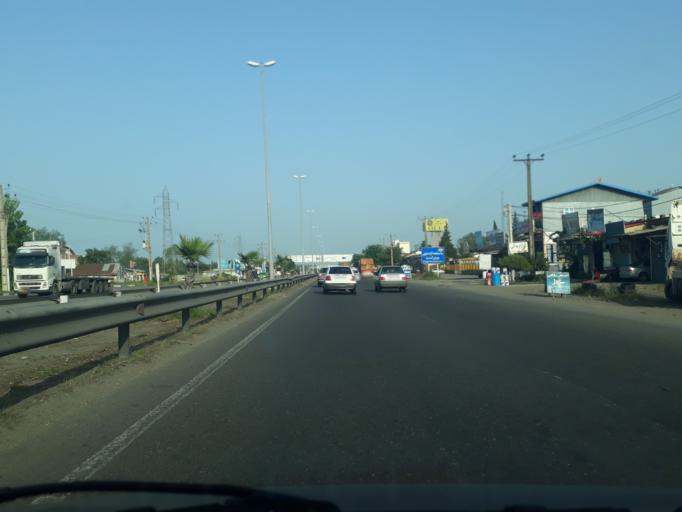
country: IR
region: Gilan
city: Bandar-e Anzali
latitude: 37.4629
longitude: 49.5555
